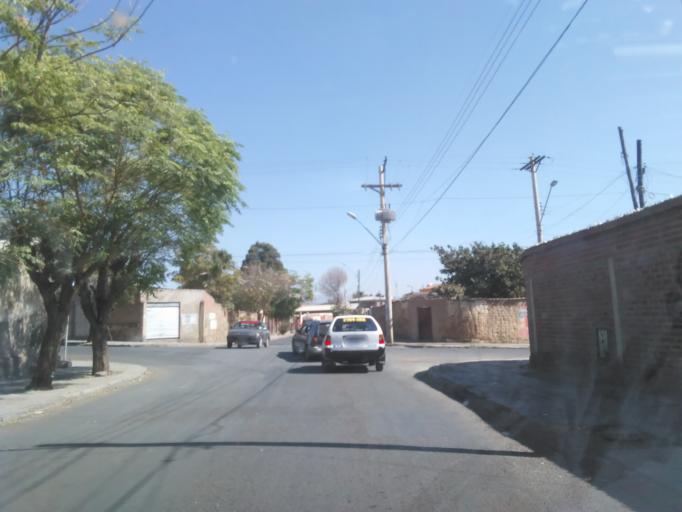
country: BO
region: Cochabamba
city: Cochabamba
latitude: -17.4120
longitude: -66.1481
